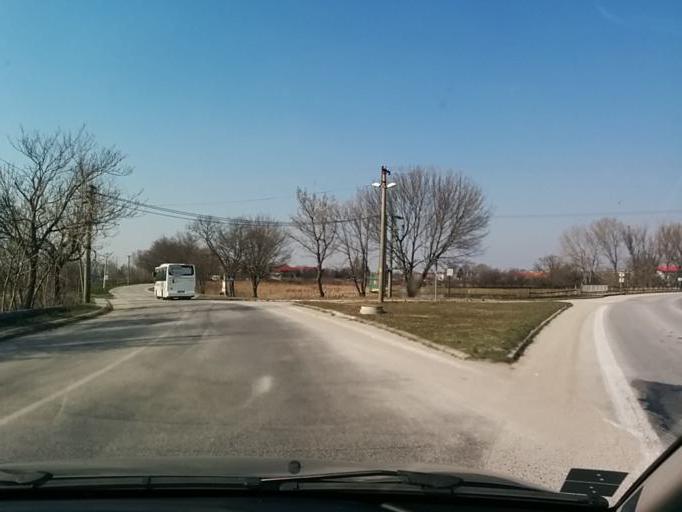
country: SK
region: Trnavsky
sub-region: Okres Galanta
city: Galanta
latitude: 48.2213
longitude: 17.7271
